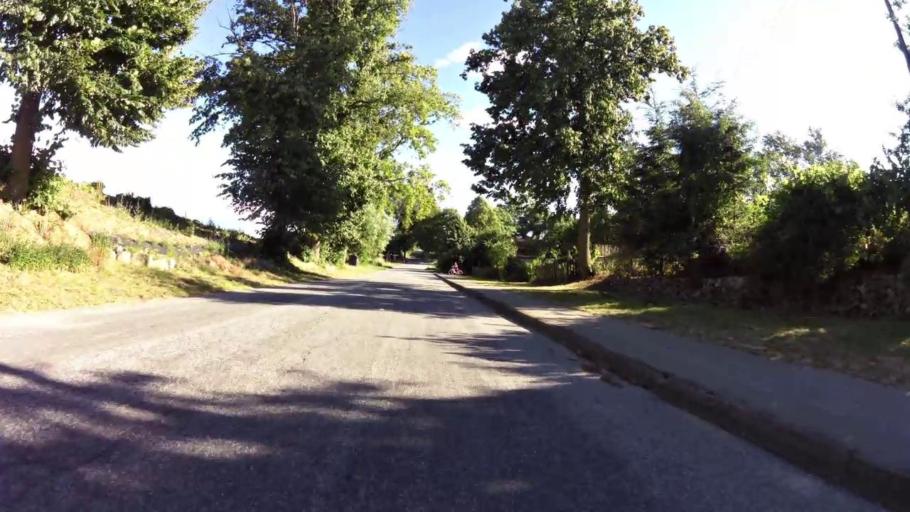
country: PL
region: West Pomeranian Voivodeship
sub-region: Powiat swidwinski
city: Swidwin
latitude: 53.7573
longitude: 15.6929
